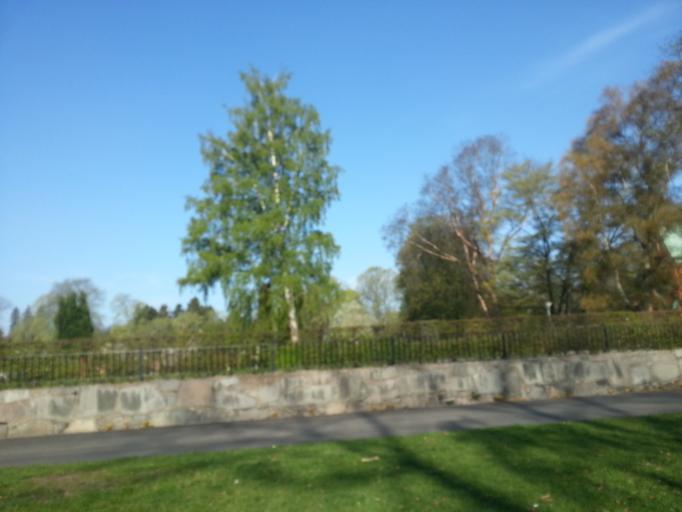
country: SE
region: OEstergoetland
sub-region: Norrkopings Kommun
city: Norrkoping
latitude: 58.5924
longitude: 16.1726
